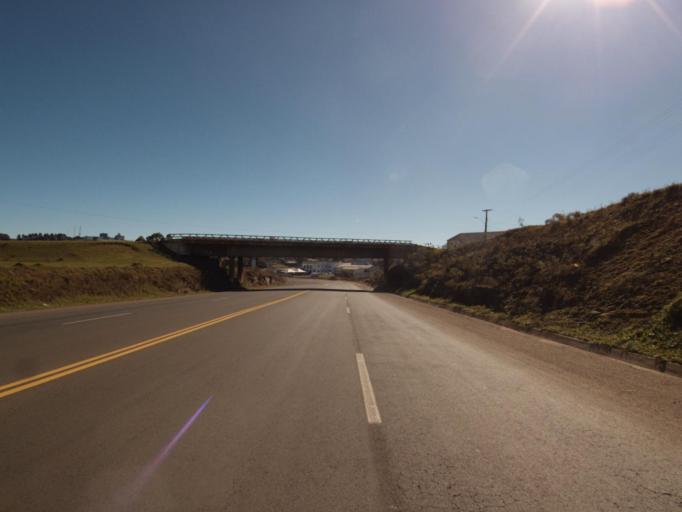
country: BR
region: Santa Catarina
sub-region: Xanxere
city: Xanxere
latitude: -26.8832
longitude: -52.4025
